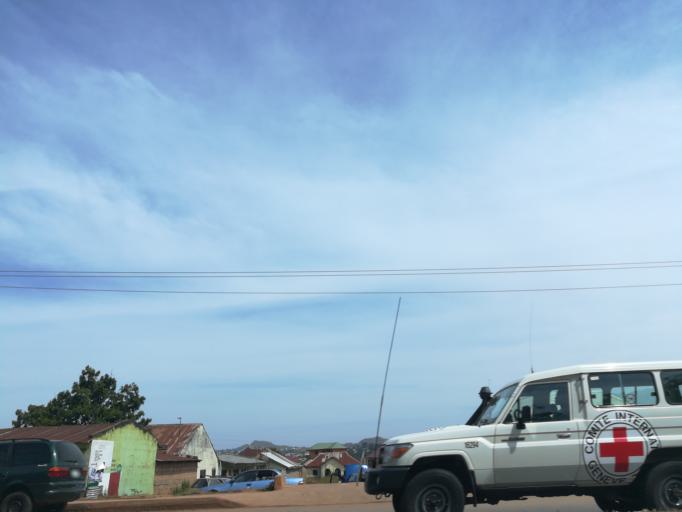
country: NG
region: Plateau
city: Bukuru
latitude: 9.7708
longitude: 8.8604
